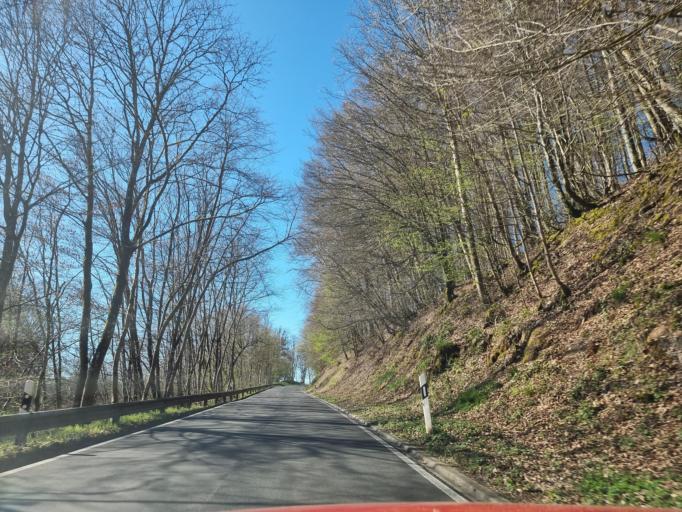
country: DE
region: Rheinland-Pfalz
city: Hosten
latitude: 49.9047
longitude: 6.6108
